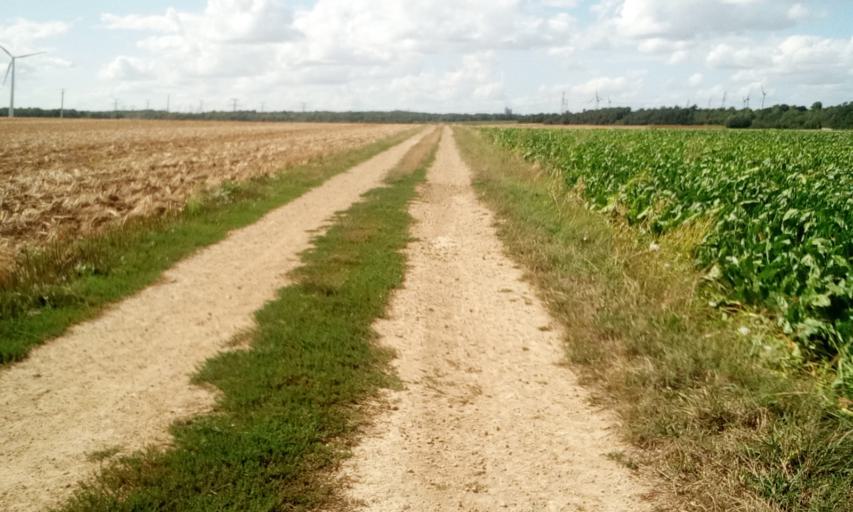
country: FR
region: Lower Normandy
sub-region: Departement du Calvados
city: Bellengreville
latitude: 49.1090
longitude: -0.2270
